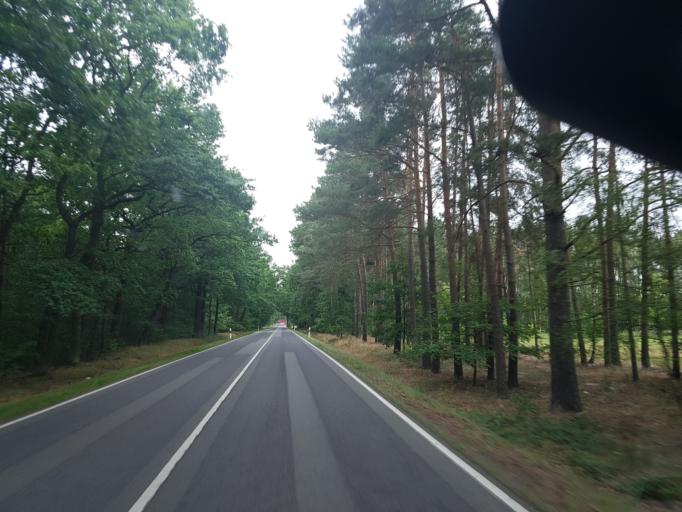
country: DE
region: Brandenburg
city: Lebusa
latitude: 51.8152
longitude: 13.4198
